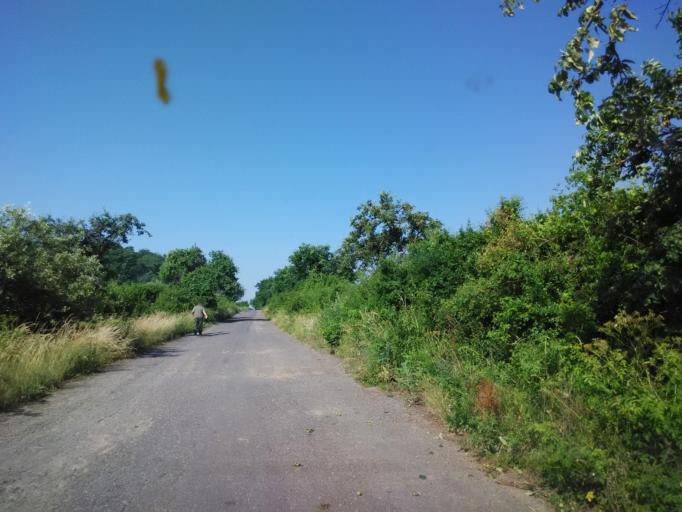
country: SK
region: Nitriansky
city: Levice
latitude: 48.2793
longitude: 18.6914
